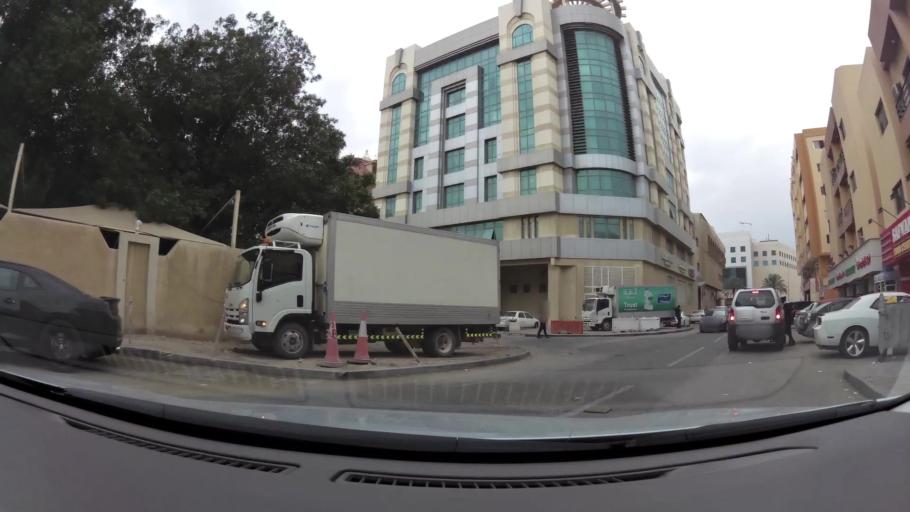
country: QA
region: Baladiyat ad Dawhah
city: Doha
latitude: 25.2799
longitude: 51.5024
